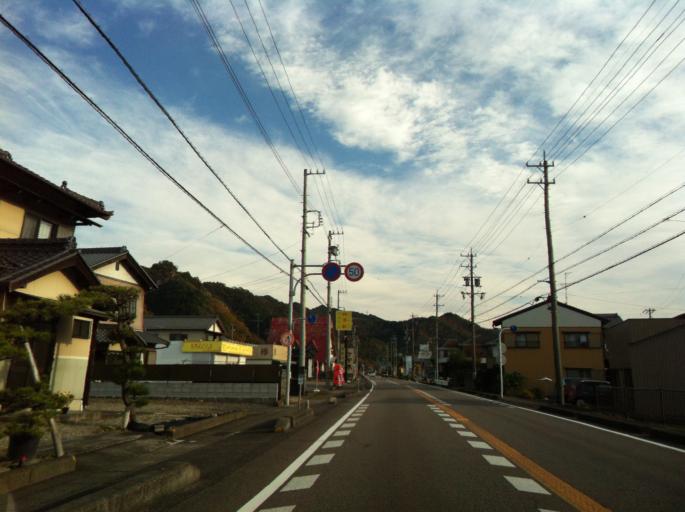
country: JP
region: Gifu
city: Minokamo
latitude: 35.5133
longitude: 137.0867
